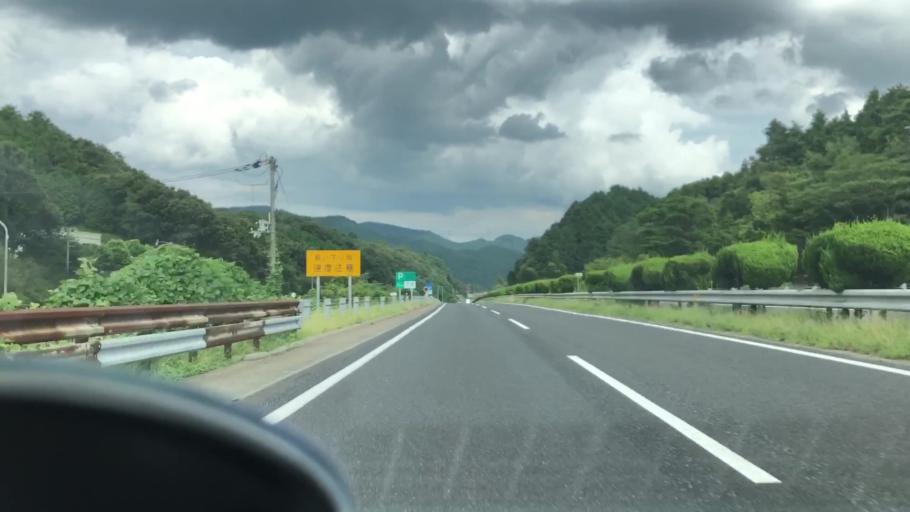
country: JP
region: Hyogo
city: Yamazakicho-nakabirose
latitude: 34.9912
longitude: 134.5804
